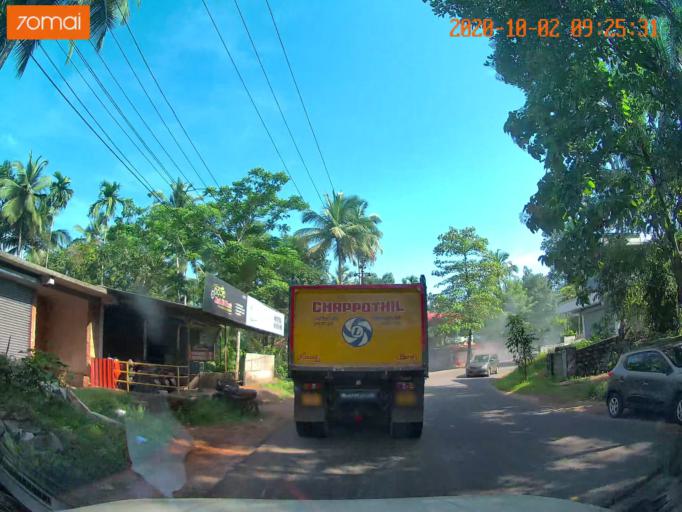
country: IN
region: Kerala
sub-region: Kozhikode
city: Naduvannur
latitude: 11.5885
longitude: 75.7654
